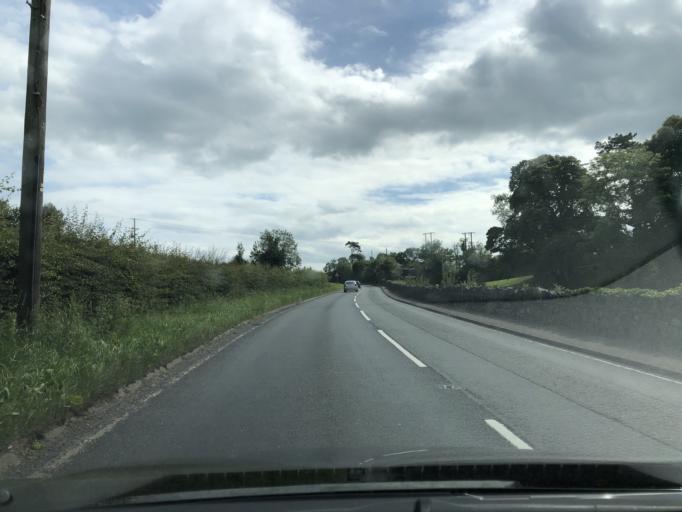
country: GB
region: Northern Ireland
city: Ballynahinch
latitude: 54.3911
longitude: -5.8833
